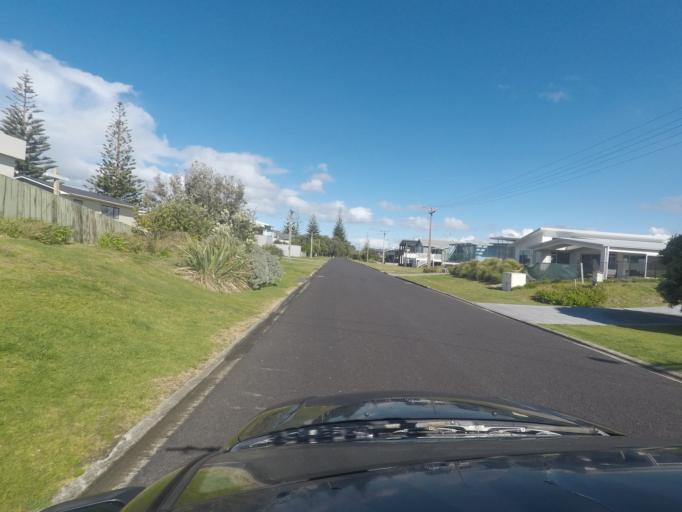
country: NZ
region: Bay of Plenty
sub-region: Western Bay of Plenty District
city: Waihi Beach
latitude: -37.4167
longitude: 175.9500
